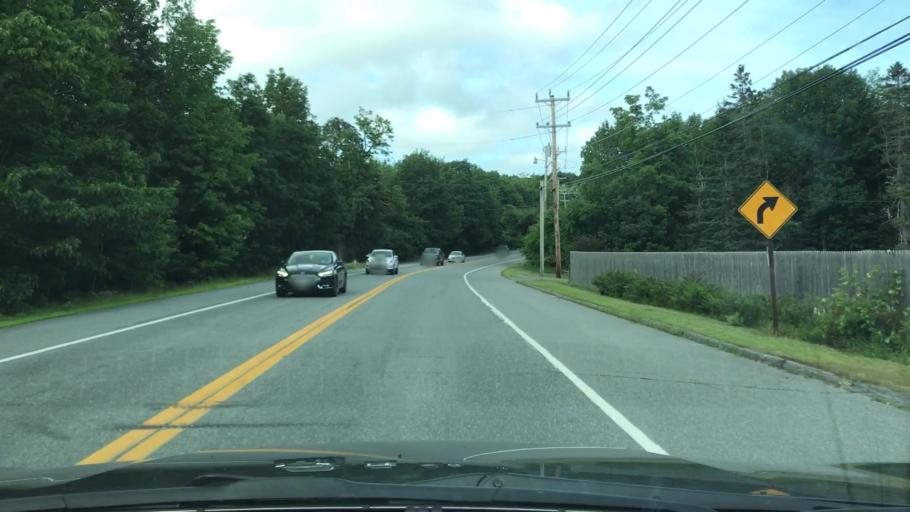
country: US
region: Maine
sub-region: Hancock County
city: Trenton
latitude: 44.4316
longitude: -68.3215
